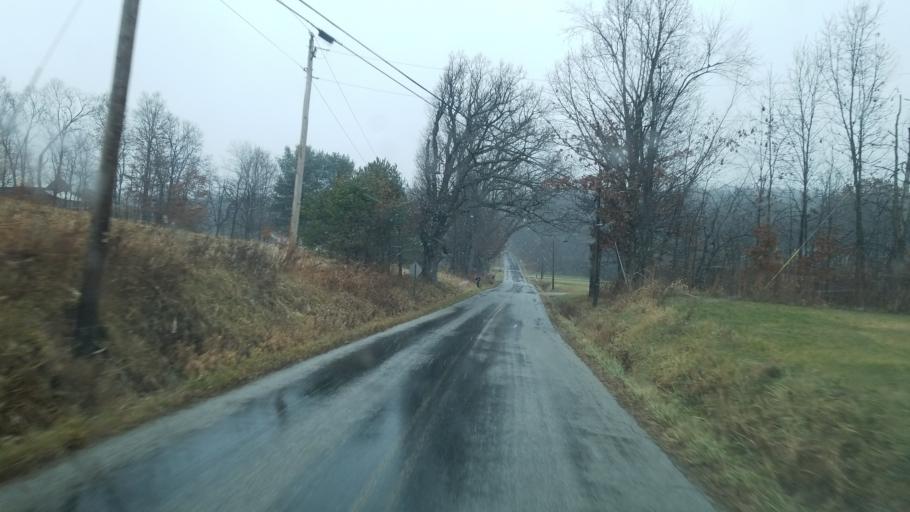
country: US
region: Ohio
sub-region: Licking County
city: Utica
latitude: 40.2163
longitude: -82.3370
